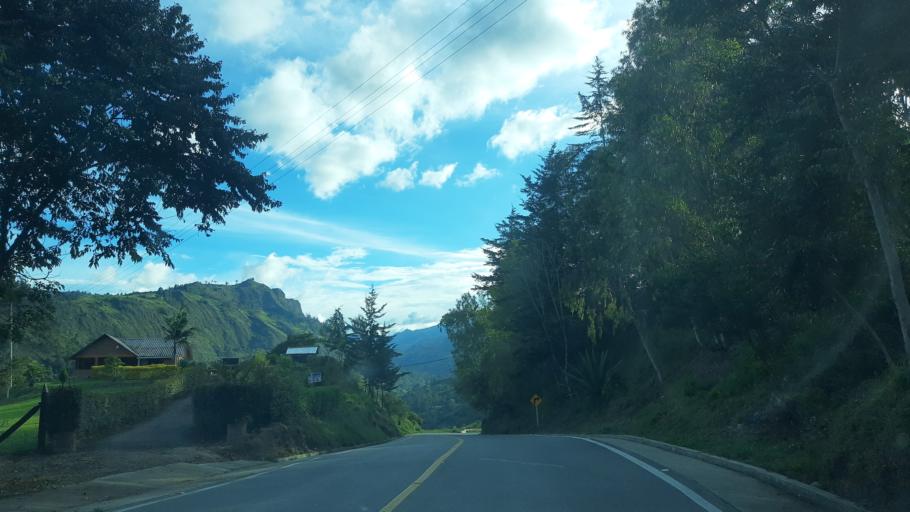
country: CO
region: Cundinamarca
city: Macheta
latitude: 5.0760
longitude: -73.5955
